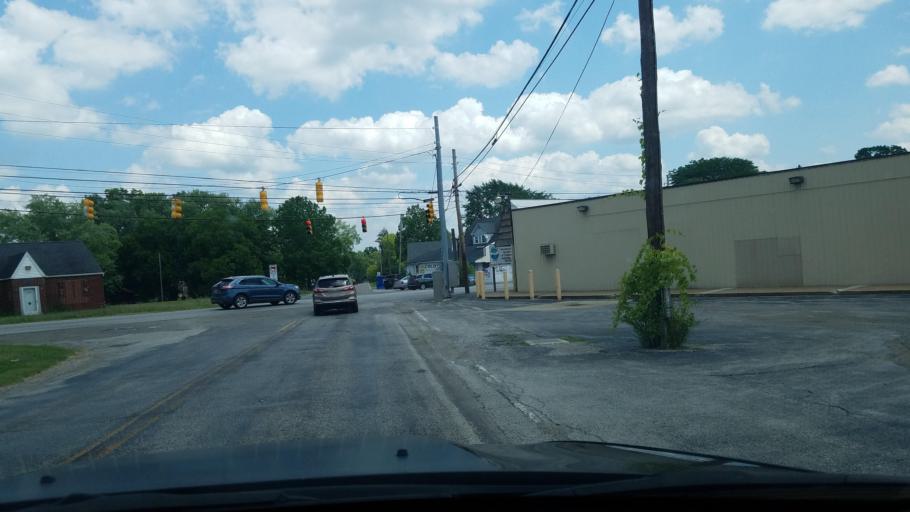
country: US
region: Ohio
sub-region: Trumbull County
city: Bolindale
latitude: 41.2032
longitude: -80.7801
